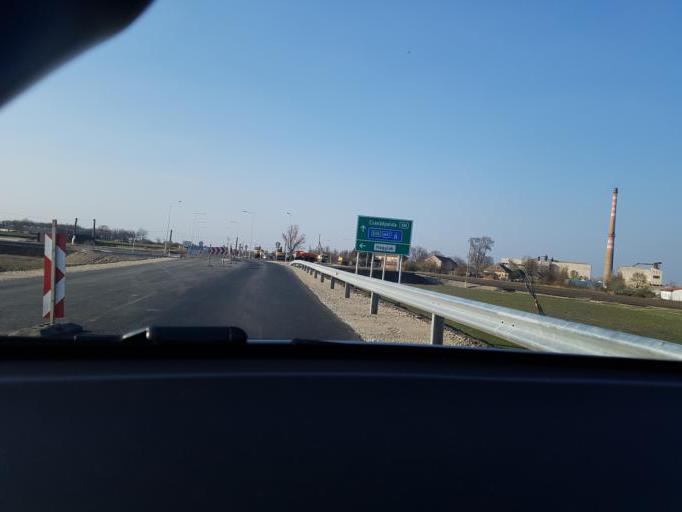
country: RO
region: Arad
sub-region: Comuna Nadlac
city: Nadlac
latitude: 46.1854
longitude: 20.7182
